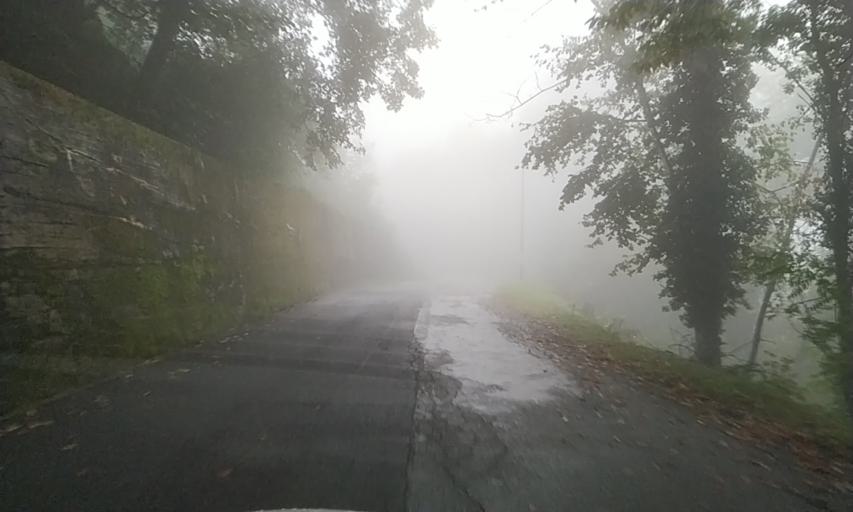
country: IT
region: Piedmont
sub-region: Provincia di Vercelli
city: Civiasco
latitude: 45.8296
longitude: 8.2811
